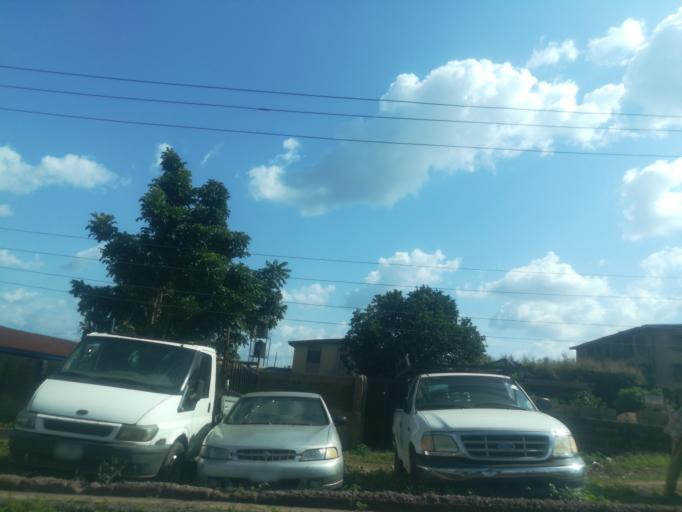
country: NG
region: Oyo
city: Egbeda
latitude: 7.4275
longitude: 3.9987
